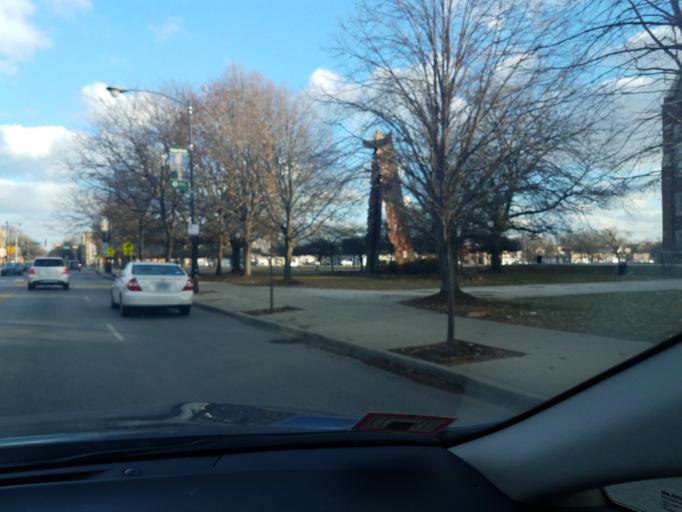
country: US
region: Illinois
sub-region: Cook County
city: Lincolnwood
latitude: 41.9467
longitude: -87.6901
